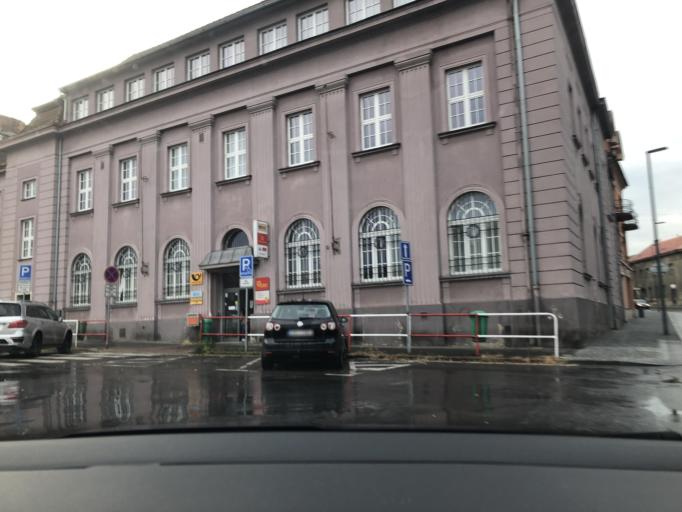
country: CZ
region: Central Bohemia
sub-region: Okres Kolin
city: Kolin
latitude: 50.0285
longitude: 15.1973
